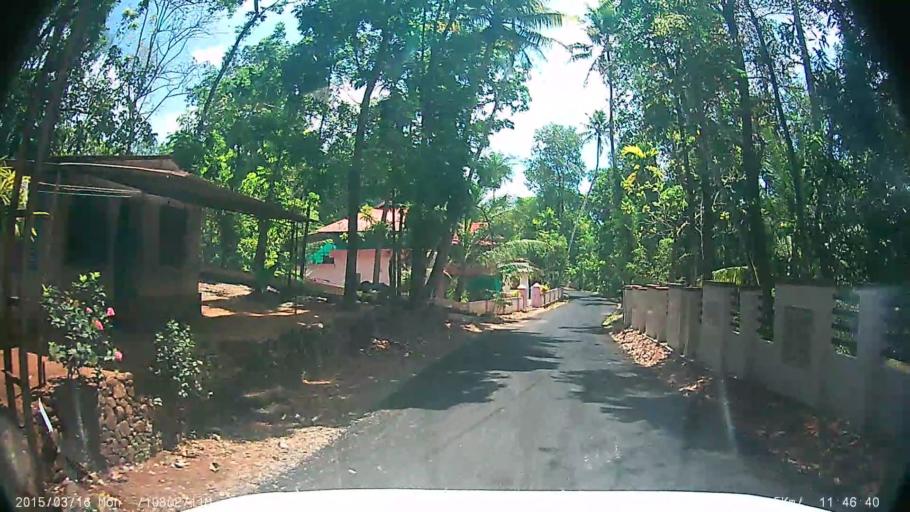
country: IN
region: Kerala
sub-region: Ernakulam
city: Piravam
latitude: 9.7957
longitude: 76.5358
